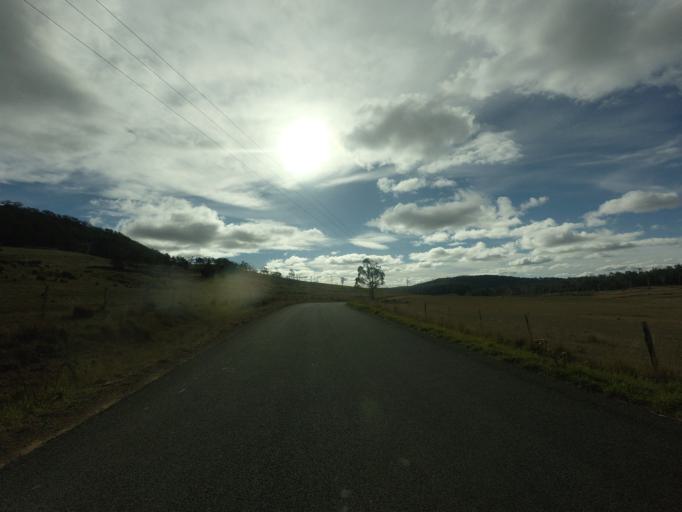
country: AU
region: Tasmania
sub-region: Brighton
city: Bridgewater
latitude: -42.3852
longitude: 147.3613
